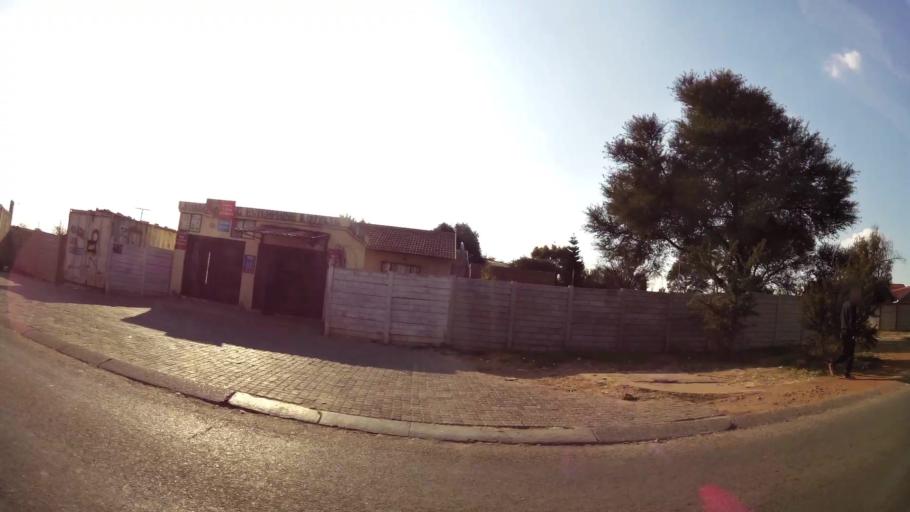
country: ZA
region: Gauteng
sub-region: Ekurhuleni Metropolitan Municipality
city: Tembisa
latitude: -25.9545
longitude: 28.2158
